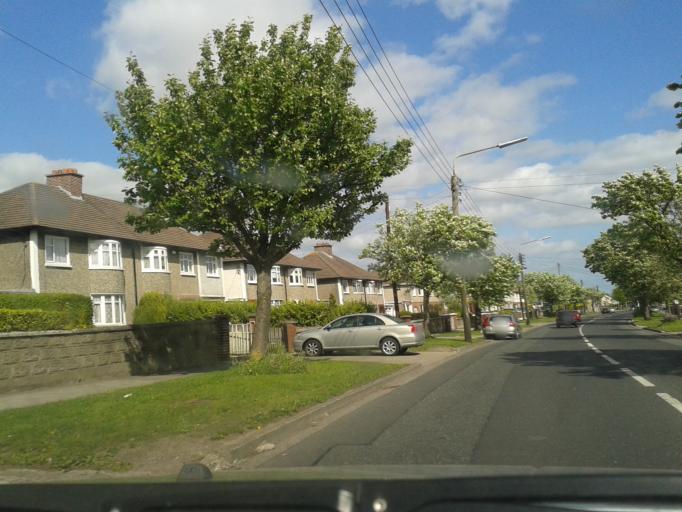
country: IE
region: Leinster
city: Ballymun
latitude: 53.3898
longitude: -6.2682
